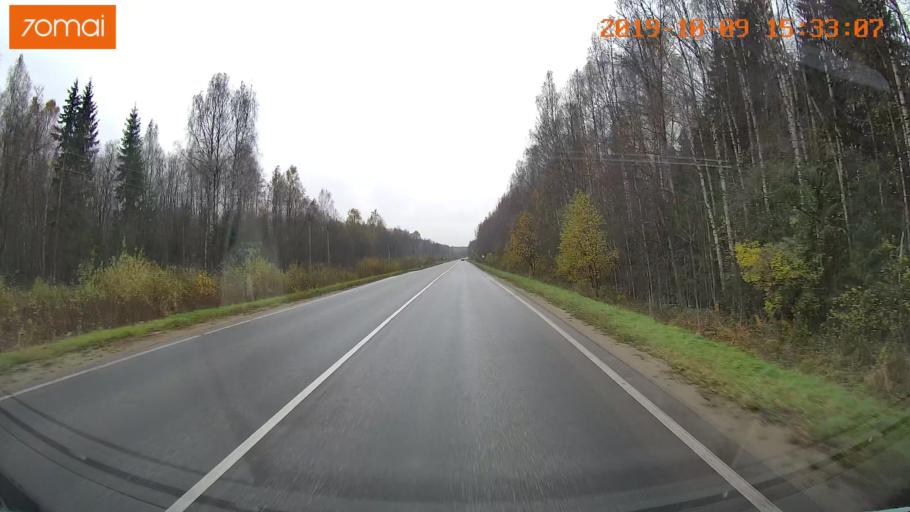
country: RU
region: Kostroma
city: Oktyabr'skiy
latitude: 57.9561
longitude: 41.2668
